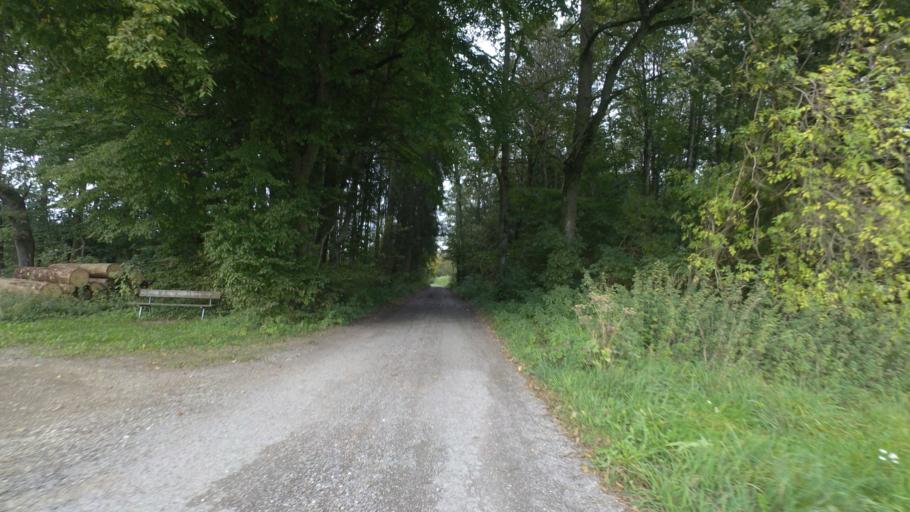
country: DE
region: Bavaria
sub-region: Upper Bavaria
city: Chieming
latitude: 47.9133
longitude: 12.5412
